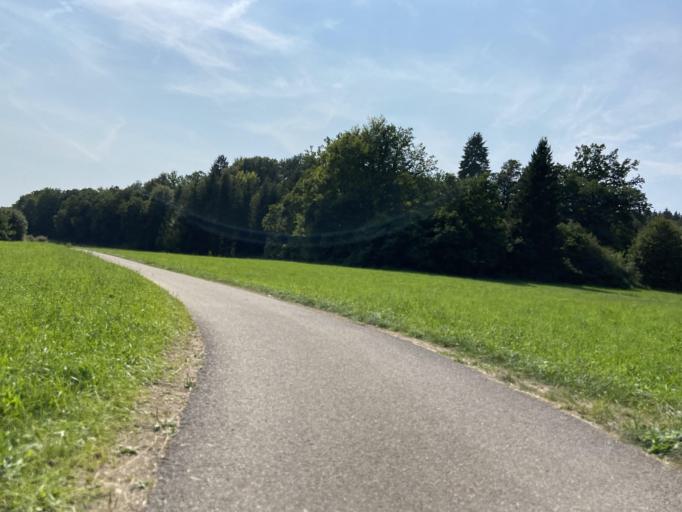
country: DE
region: Baden-Wuerttemberg
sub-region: Tuebingen Region
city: Bingen
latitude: 48.0976
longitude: 9.2823
